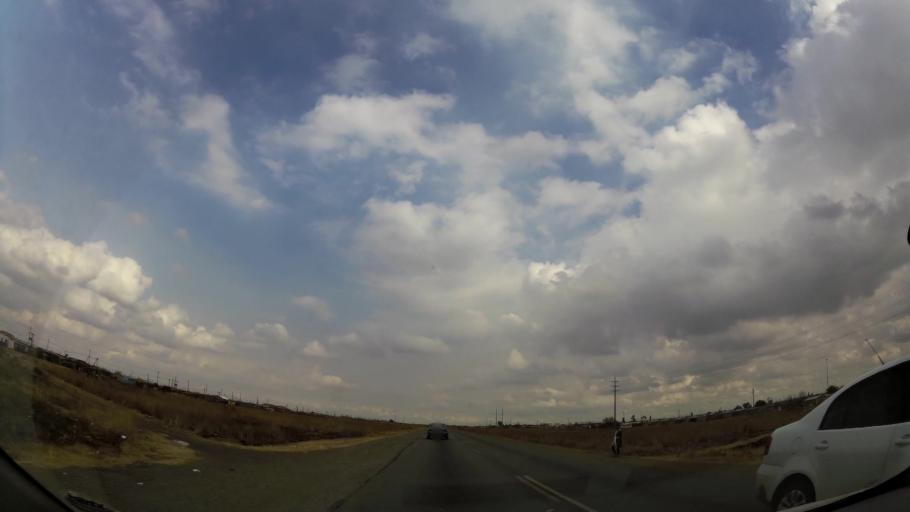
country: ZA
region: Orange Free State
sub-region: Fezile Dabi District Municipality
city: Sasolburg
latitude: -26.8515
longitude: 27.8889
